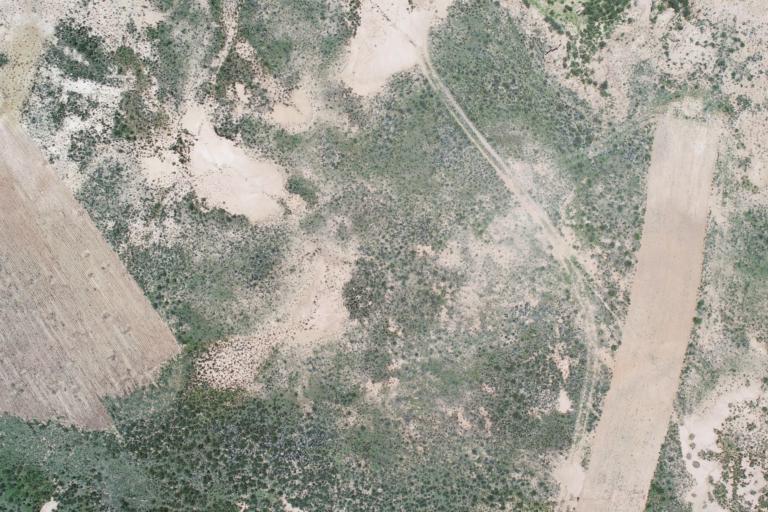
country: BO
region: La Paz
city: Curahuara de Carangas
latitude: -17.3293
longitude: -68.5135
